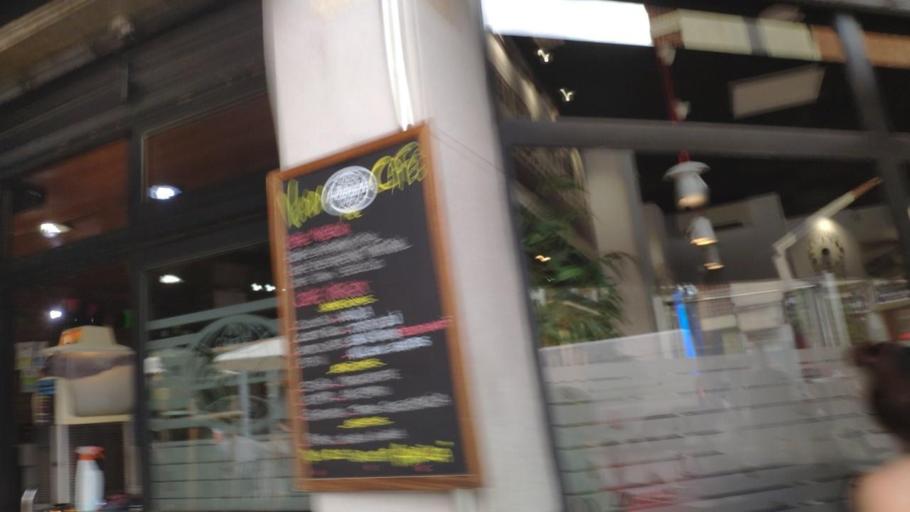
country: ES
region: Catalonia
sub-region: Provincia de Barcelona
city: Sant Cugat del Valles
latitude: 41.4738
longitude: 2.0899
